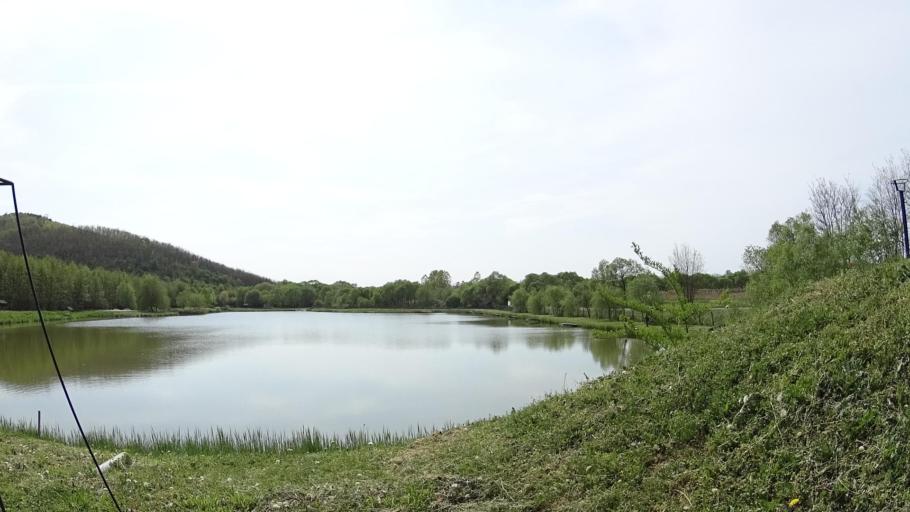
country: HU
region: Nograd
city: Romhany
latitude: 47.9425
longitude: 19.2983
